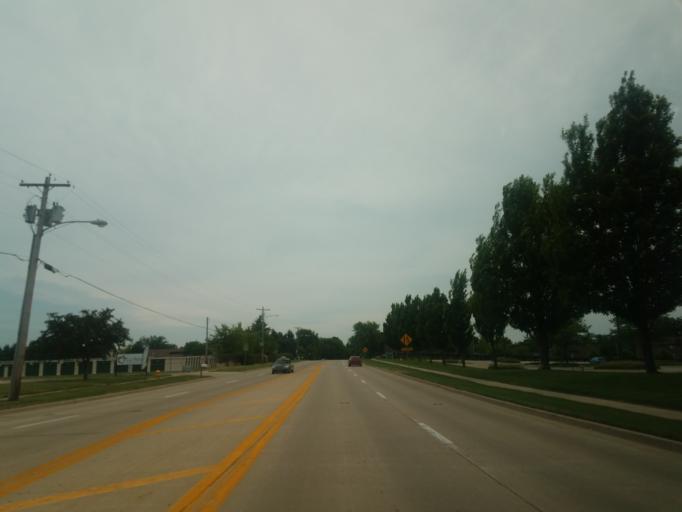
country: US
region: Illinois
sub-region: McLean County
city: Normal
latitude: 40.5014
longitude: -88.9388
